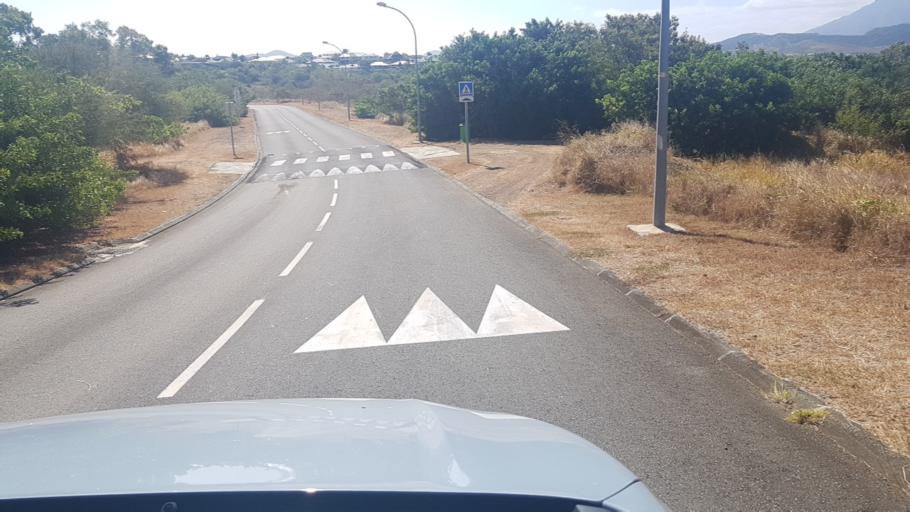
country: NC
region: South Province
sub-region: Dumbea
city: Dumbea
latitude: -22.1949
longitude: 166.4311
